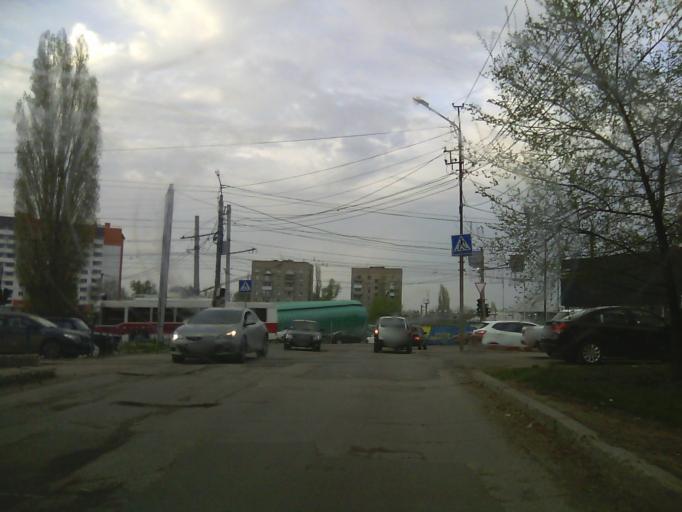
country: RU
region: Saratov
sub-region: Saratovskiy Rayon
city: Saratov
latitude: 51.5912
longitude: 45.9376
